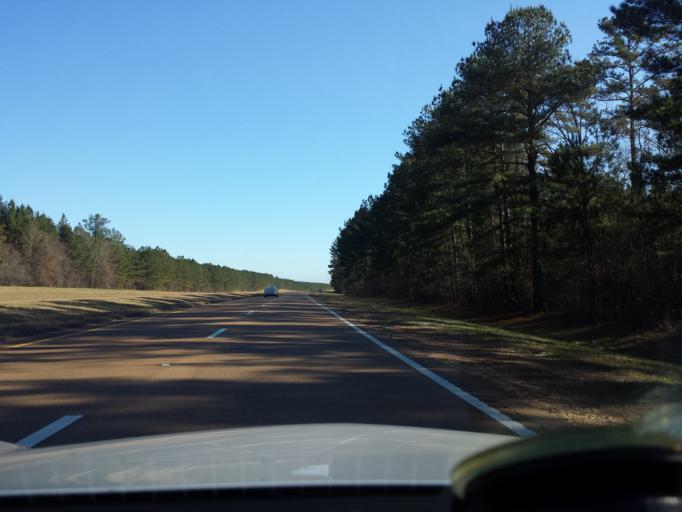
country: US
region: Mississippi
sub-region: Rankin County
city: Pelahatchie
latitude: 32.5404
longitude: -89.8092
